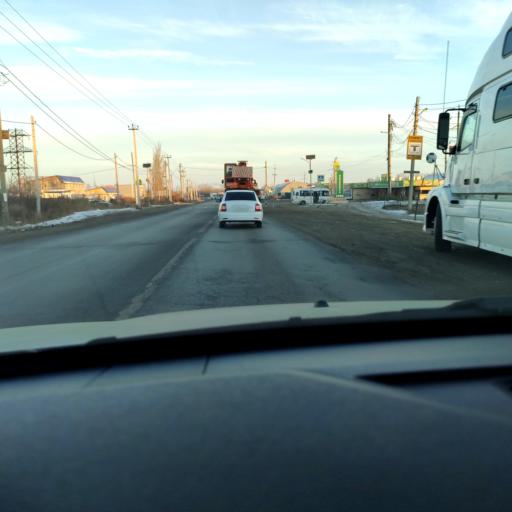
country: RU
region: Samara
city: Smyshlyayevka
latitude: 53.2520
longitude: 50.4751
